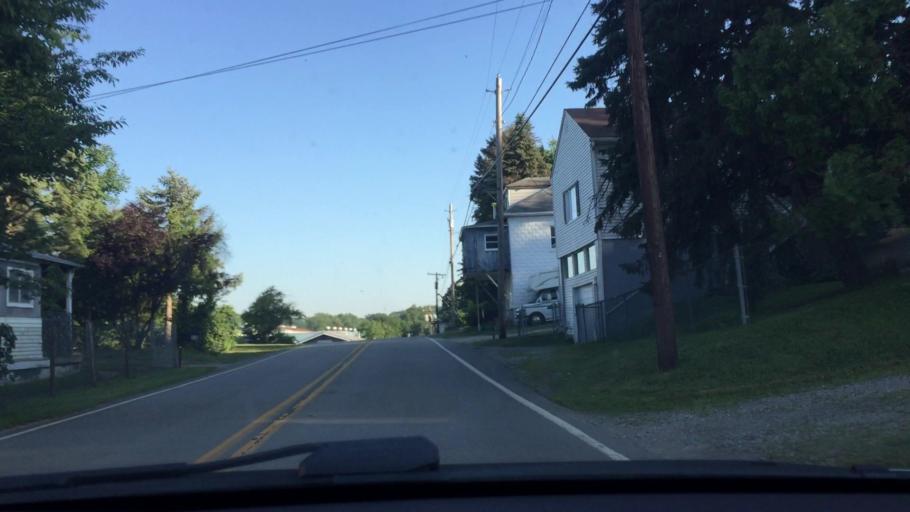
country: US
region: Pennsylvania
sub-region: Washington County
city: East Washington
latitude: 40.1939
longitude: -80.2181
